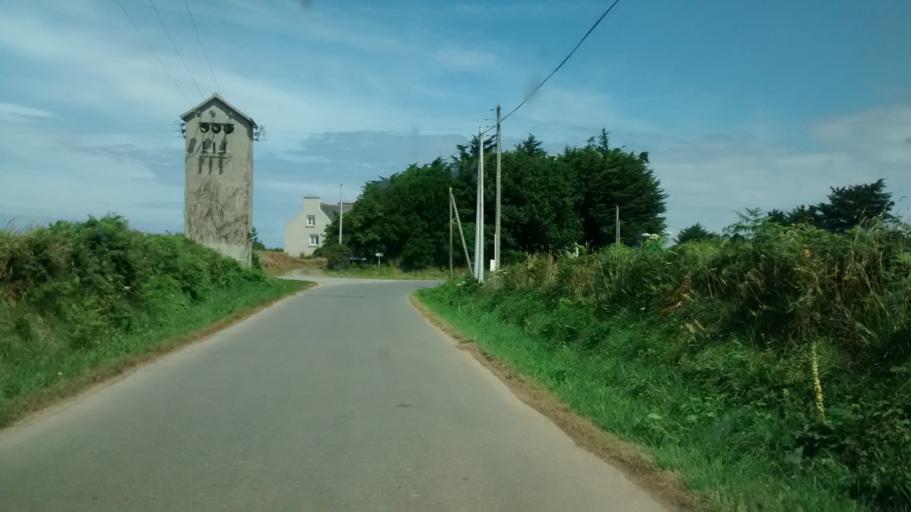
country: FR
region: Brittany
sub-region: Departement du Finistere
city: Plouguerneau
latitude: 48.6155
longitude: -4.4804
